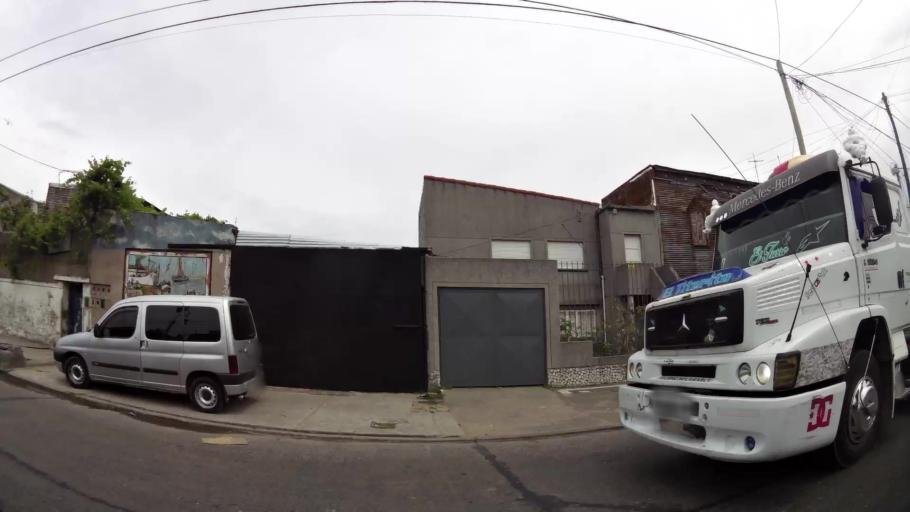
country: AR
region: Buenos Aires
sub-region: Partido de Avellaneda
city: Avellaneda
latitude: -34.6560
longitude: -58.3480
